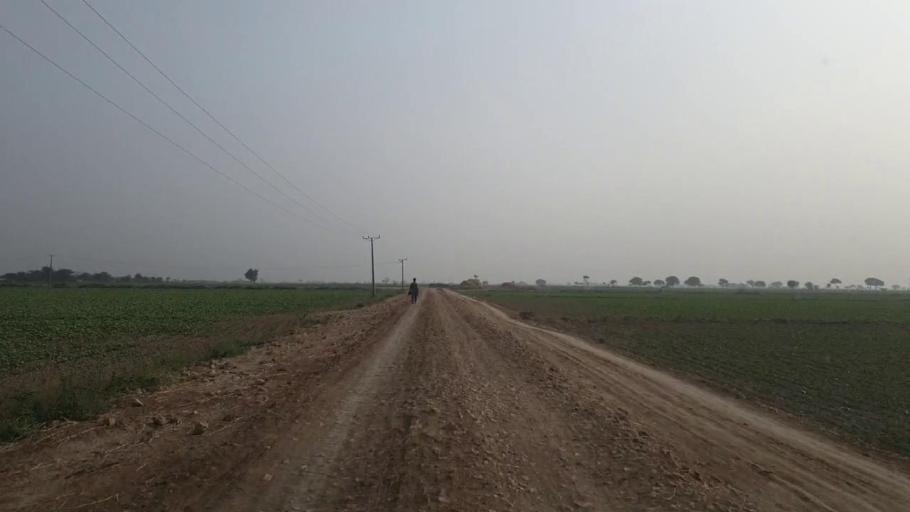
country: PK
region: Sindh
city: Mirpur Batoro
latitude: 24.5607
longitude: 68.4186
